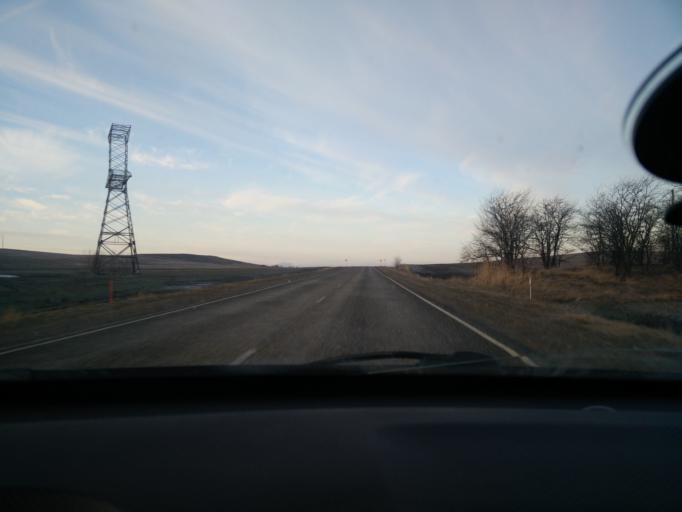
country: RU
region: Stavropol'skiy
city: Balakhonovskoye
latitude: 44.9925
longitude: 41.7137
